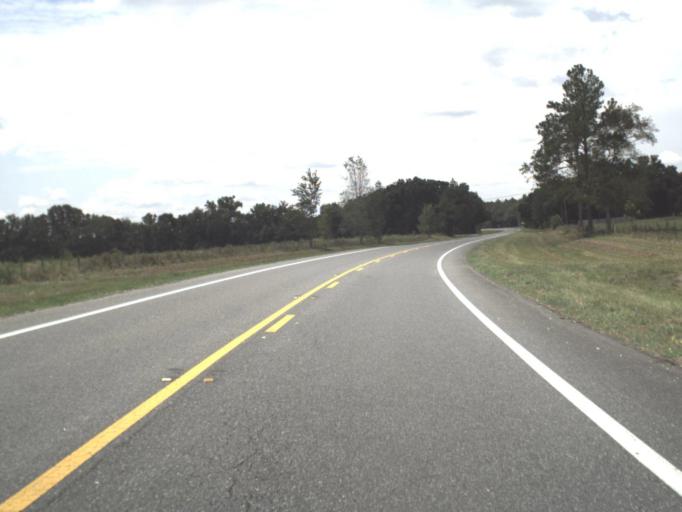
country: US
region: Florida
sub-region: Suwannee County
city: Live Oak
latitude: 30.1489
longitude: -82.9495
